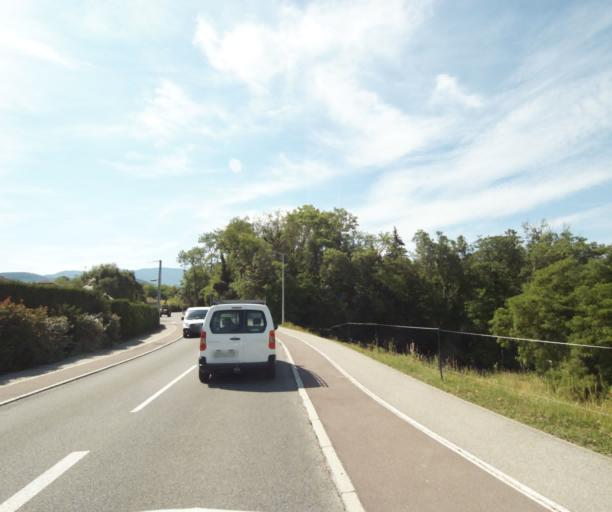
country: FR
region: Rhone-Alpes
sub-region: Departement de la Haute-Savoie
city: Margencel
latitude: 46.3400
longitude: 6.4159
